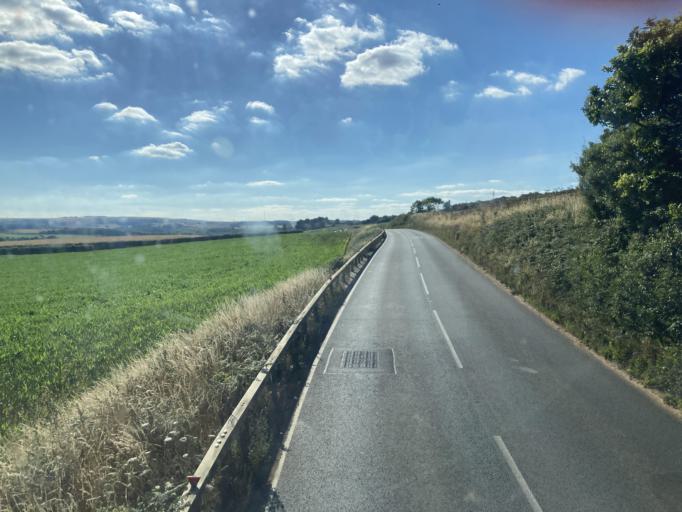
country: GB
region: England
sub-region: Isle of Wight
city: Newport
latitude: 50.6708
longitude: -1.2592
